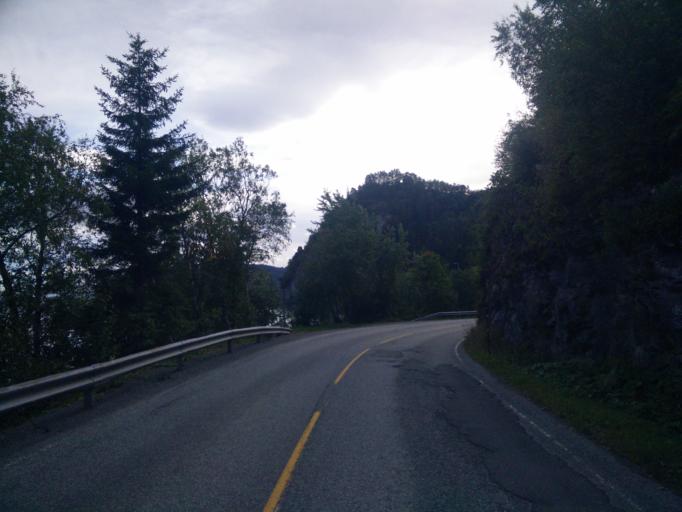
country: NO
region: Sor-Trondelag
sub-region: Skaun
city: Borsa
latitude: 63.3243
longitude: 10.1182
